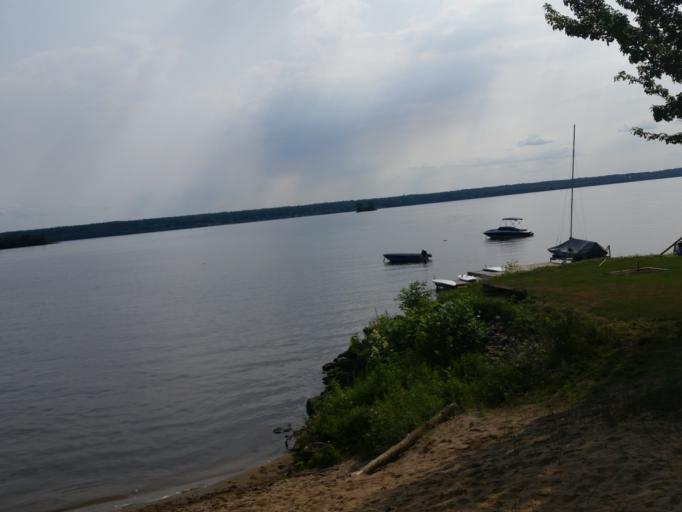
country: CA
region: Ontario
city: Arnprior
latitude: 45.5135
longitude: -76.4065
